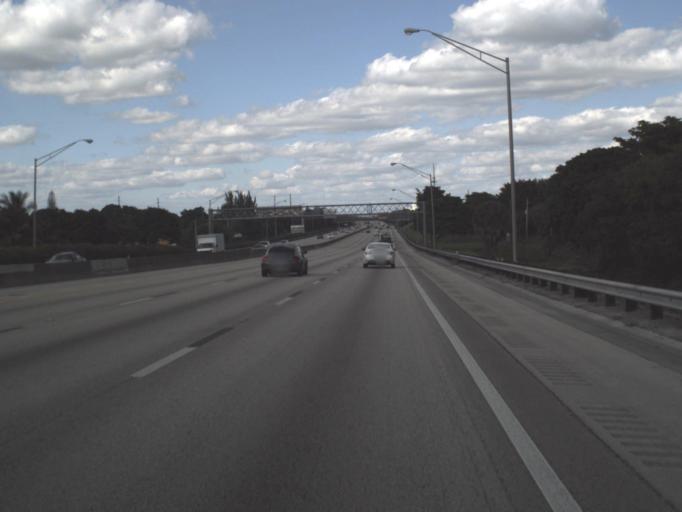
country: US
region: Florida
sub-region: Broward County
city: Pembroke Pines
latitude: 26.0267
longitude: -80.2131
